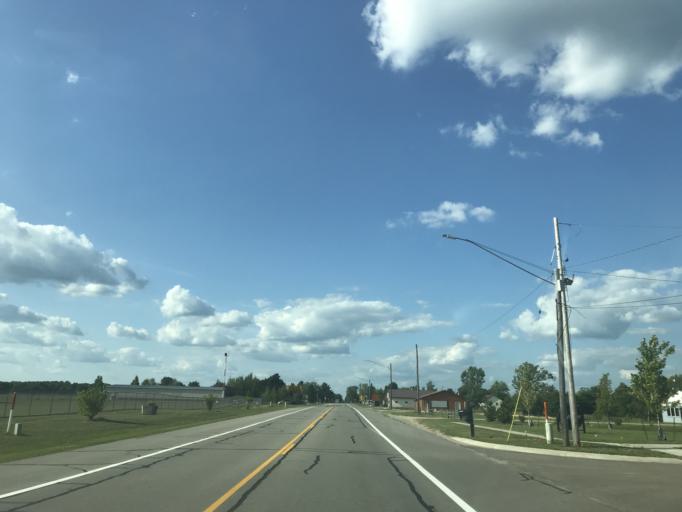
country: US
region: Michigan
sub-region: Newaygo County
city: White Cloud
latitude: 43.5569
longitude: -85.7716
